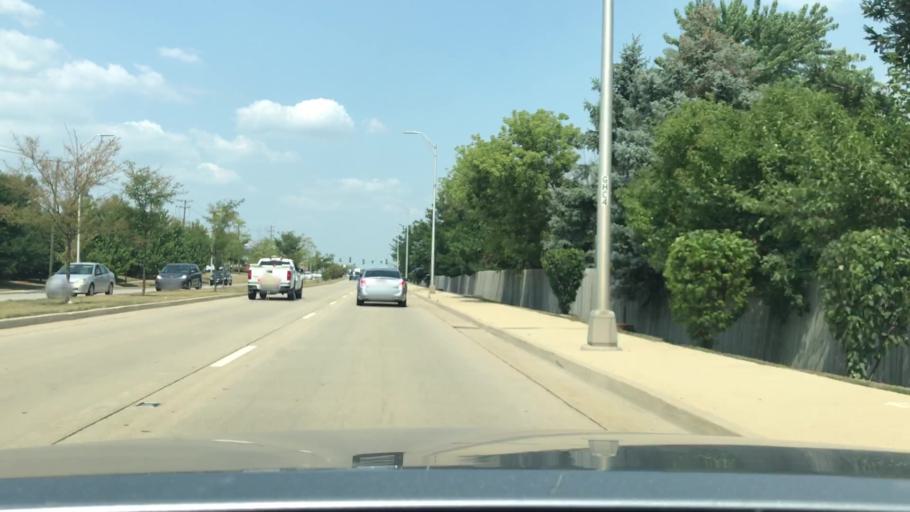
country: US
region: Illinois
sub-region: Will County
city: Shorewood
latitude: 41.5578
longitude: -88.2000
